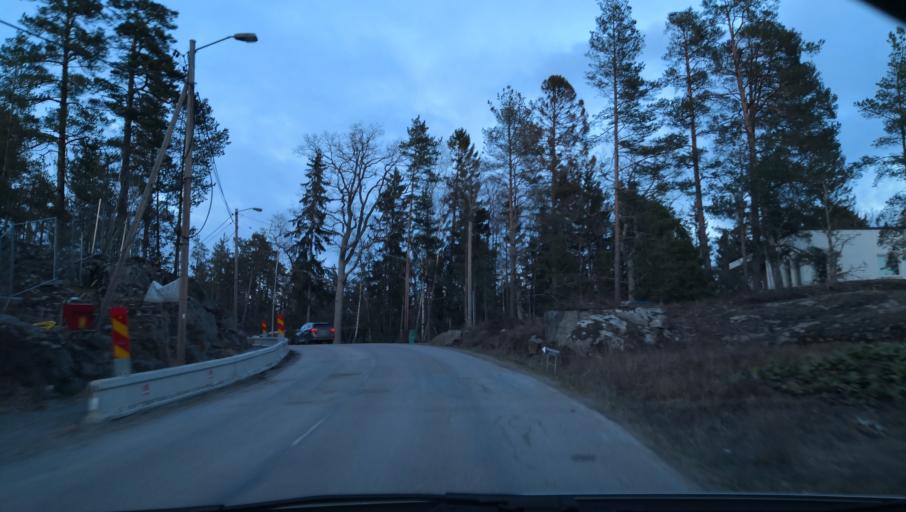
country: SE
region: Stockholm
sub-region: Nacka Kommun
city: Kummelnas
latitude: 59.3515
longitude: 18.2914
